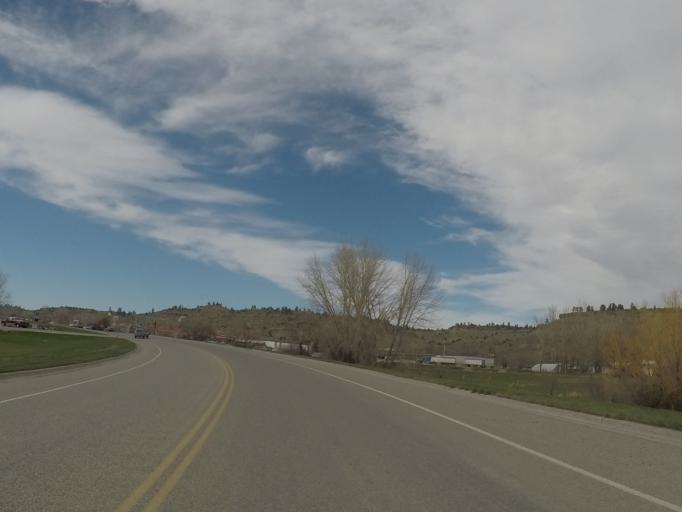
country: US
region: Montana
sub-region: Stillwater County
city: Columbus
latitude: 45.6411
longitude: -109.2461
